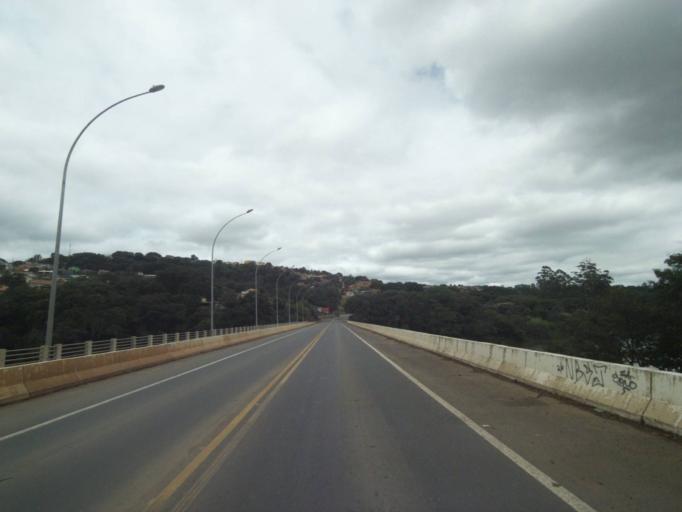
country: BR
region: Parana
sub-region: Telemaco Borba
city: Telemaco Borba
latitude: -24.3121
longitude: -50.6147
